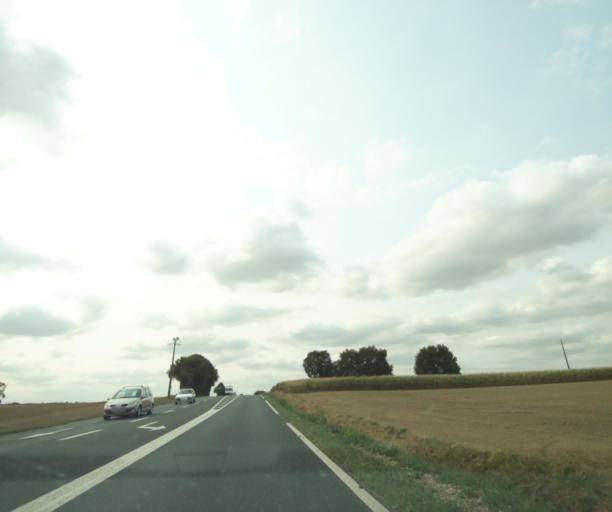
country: FR
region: Centre
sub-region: Departement de l'Indre
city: Buzancais
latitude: 46.9089
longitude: 1.3417
